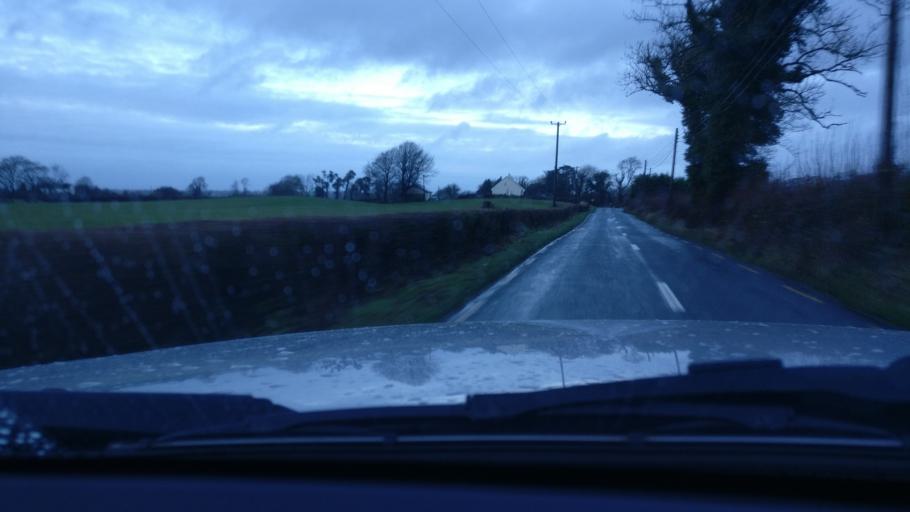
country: IE
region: Connaught
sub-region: County Galway
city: Ballinasloe
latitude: 53.2621
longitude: -8.2553
